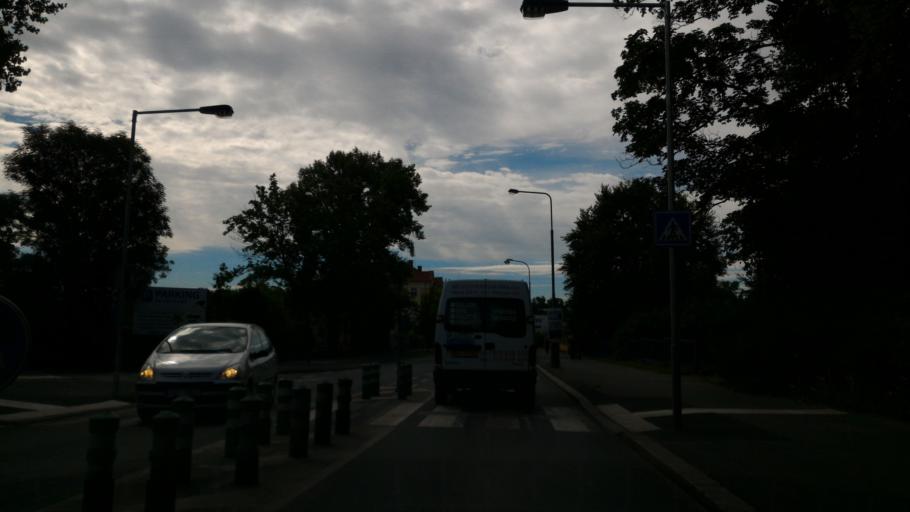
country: CZ
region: Central Bohemia
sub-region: Okres Melnik
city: Melnik
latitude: 50.3429
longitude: 14.4884
